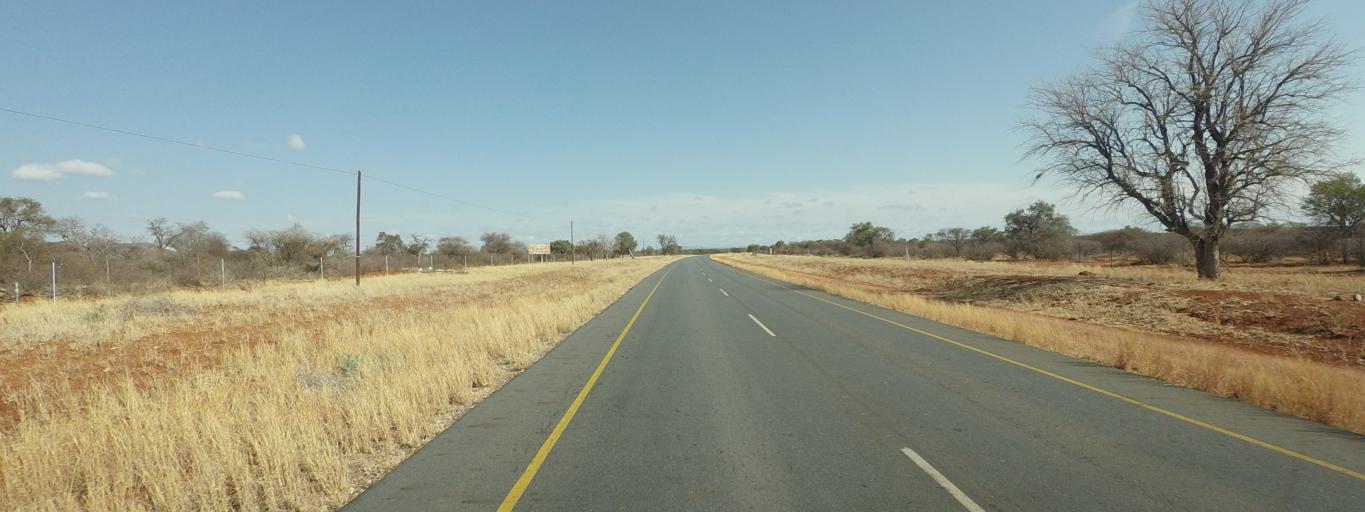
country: BW
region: Central
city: Makobeng
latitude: -22.9582
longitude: 27.9022
